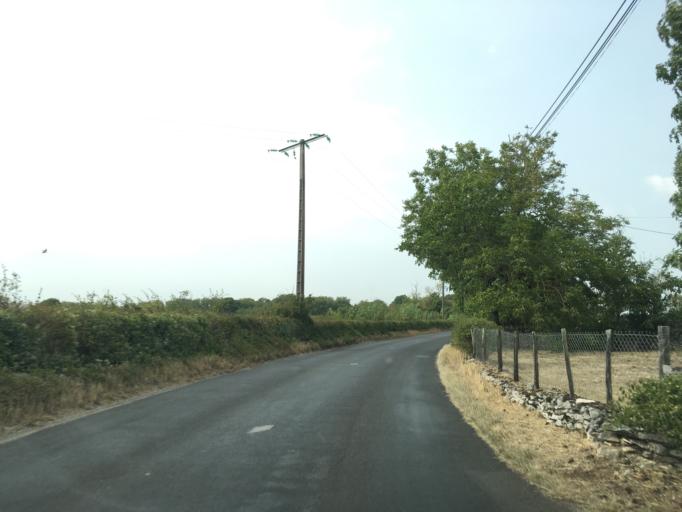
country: FR
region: Midi-Pyrenees
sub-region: Departement du Lot
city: Gramat
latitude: 44.8136
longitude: 1.6031
